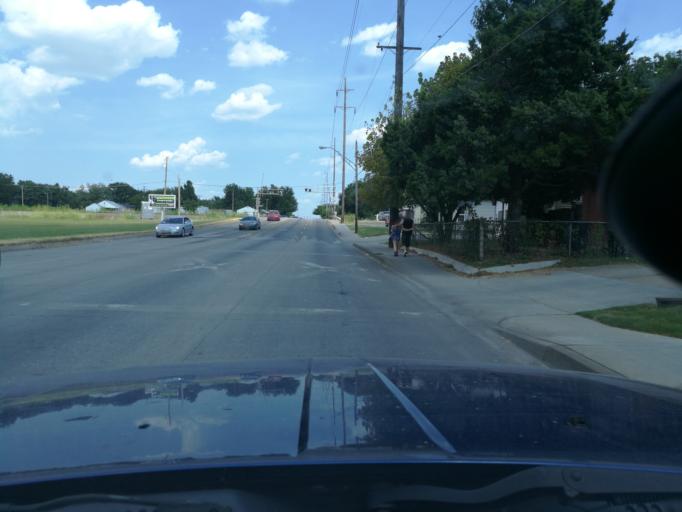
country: US
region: Oklahoma
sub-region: Oklahoma County
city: Oklahoma City
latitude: 35.4208
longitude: -97.5013
